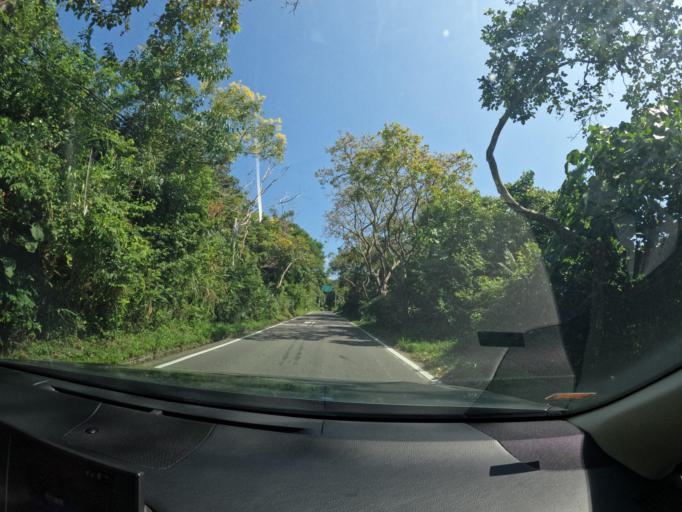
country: TW
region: Taiwan
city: Yujing
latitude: 23.1213
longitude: 120.7100
